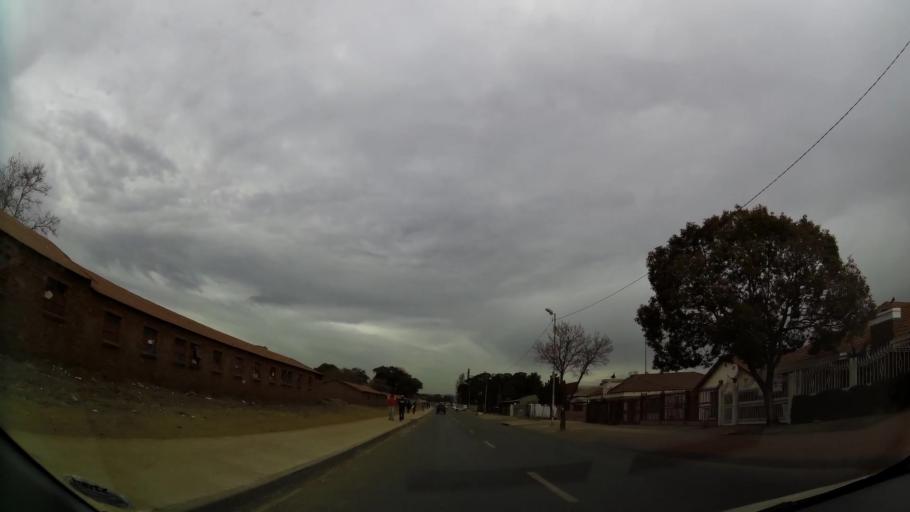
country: ZA
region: Gauteng
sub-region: City of Tshwane Metropolitan Municipality
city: Pretoria
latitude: -25.7112
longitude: 28.3300
